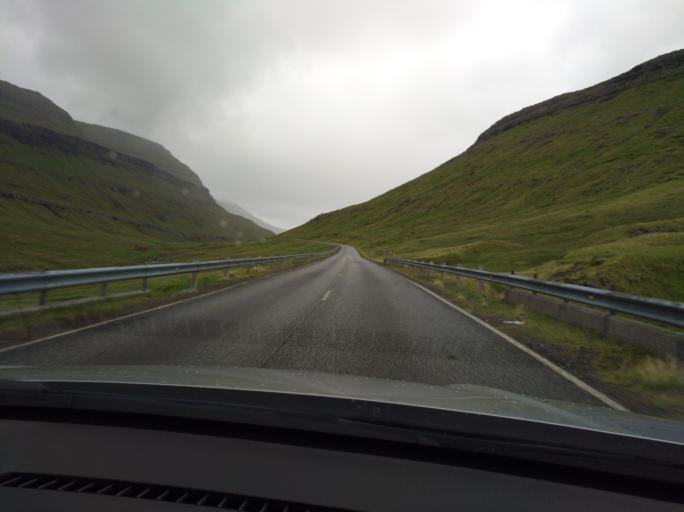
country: FO
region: Eysturoy
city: Fuglafjordur
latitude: 62.2268
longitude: -6.8792
